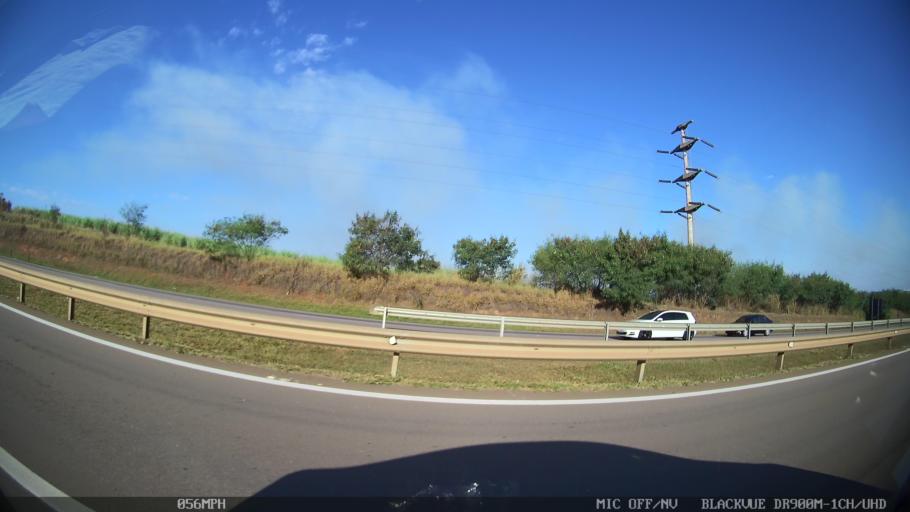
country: BR
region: Sao Paulo
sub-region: Piracicaba
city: Piracicaba
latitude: -22.6837
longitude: -47.5958
